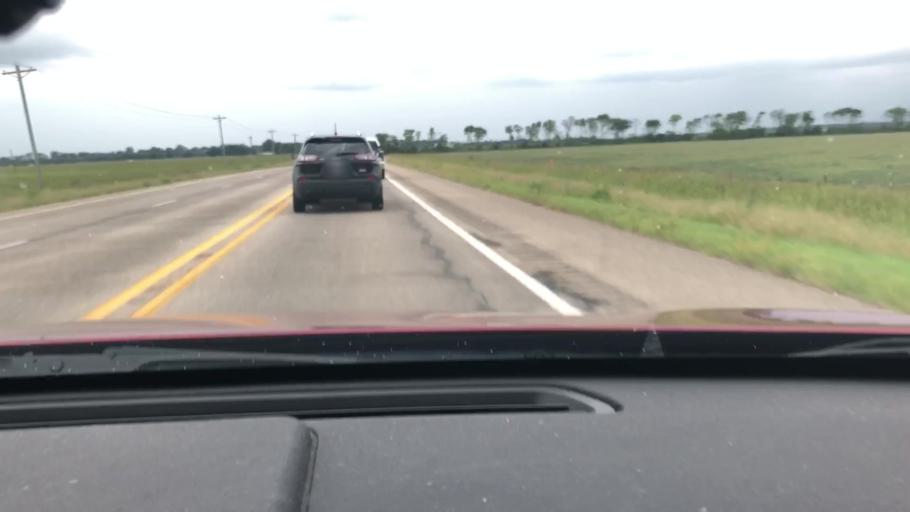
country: US
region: Arkansas
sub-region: Lafayette County
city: Lewisville
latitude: 33.3857
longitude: -93.7361
